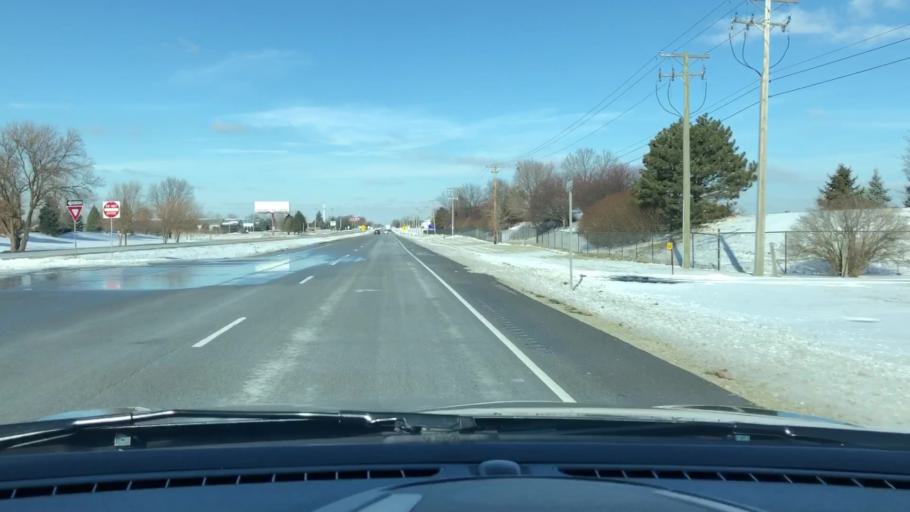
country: US
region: Illinois
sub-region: Will County
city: Preston Heights
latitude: 41.4625
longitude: -88.0794
